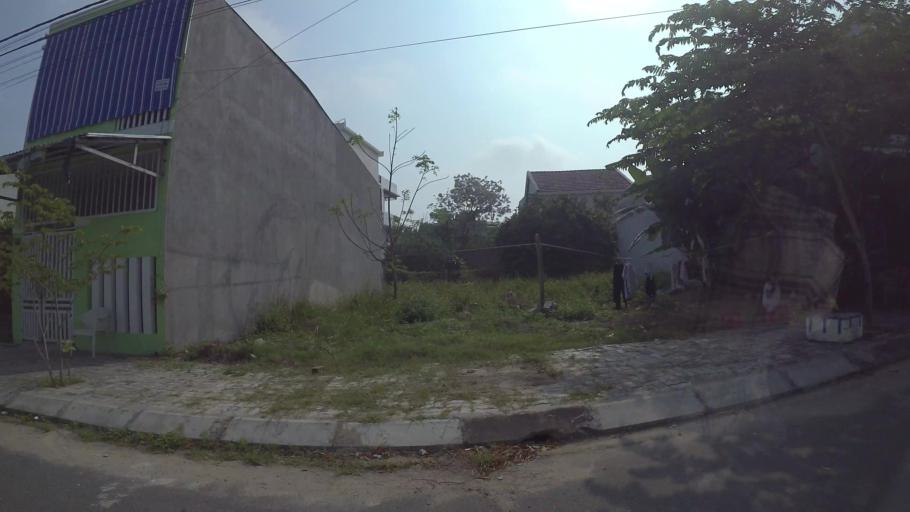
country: VN
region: Da Nang
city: Ngu Hanh Son
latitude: 16.0291
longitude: 108.2436
